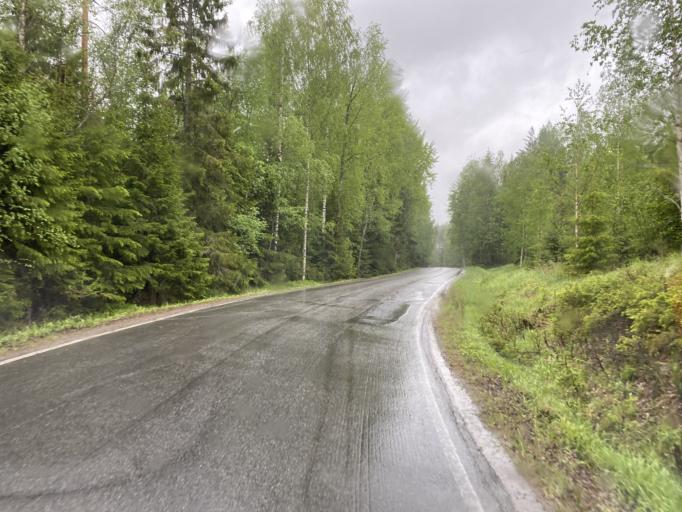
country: FI
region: Haeme
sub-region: Forssa
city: Humppila
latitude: 61.0909
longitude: 23.3123
